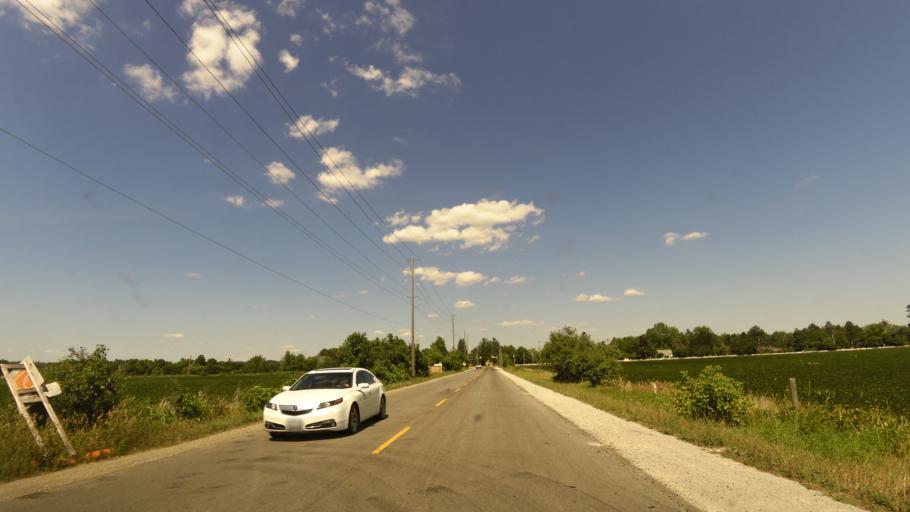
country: CA
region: Ontario
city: Brampton
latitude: 43.6408
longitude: -79.8595
